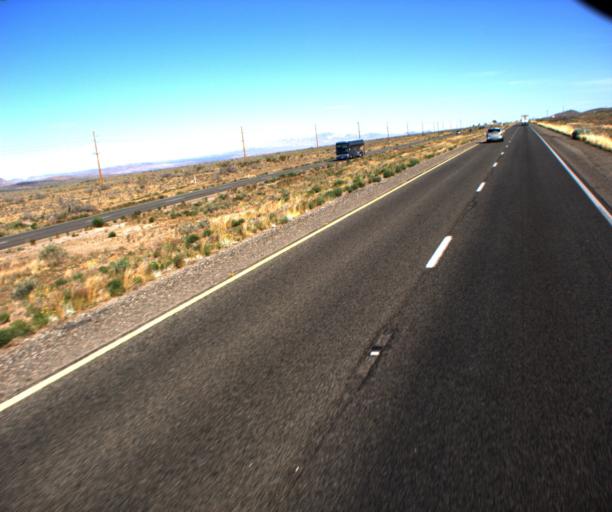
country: US
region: Arizona
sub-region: Mohave County
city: Golden Valley
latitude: 35.3856
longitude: -114.2509
